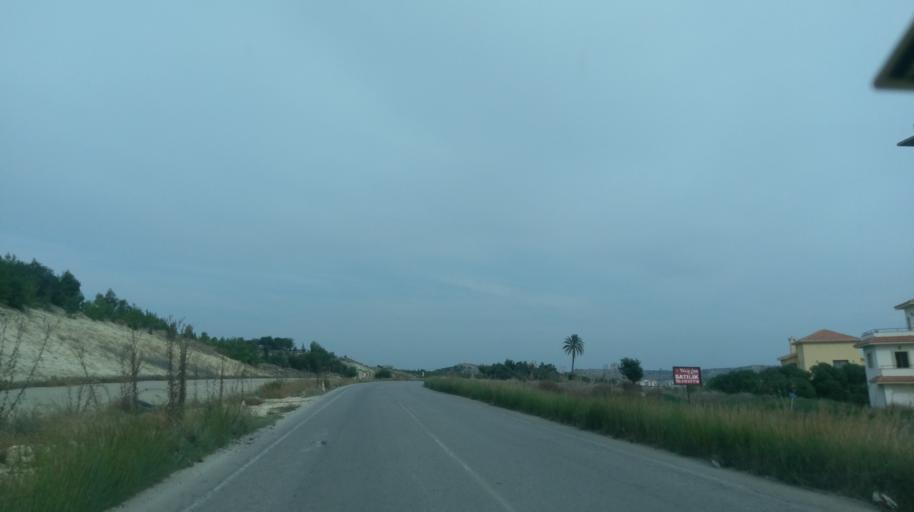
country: CY
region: Ammochostos
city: Trikomo
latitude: 35.3348
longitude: 33.9791
